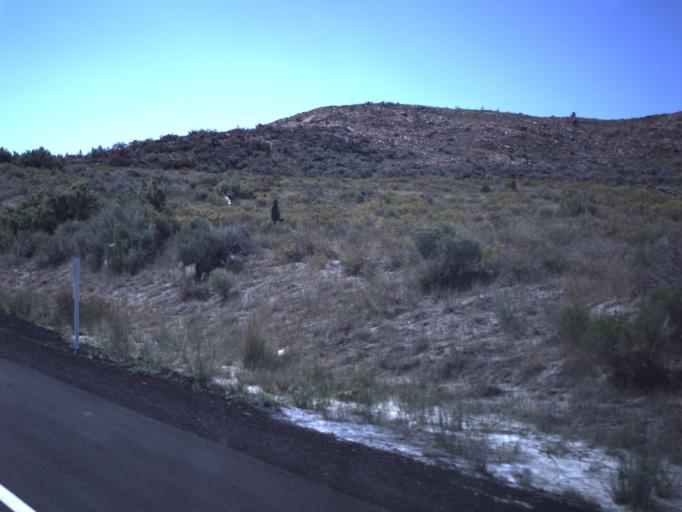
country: US
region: Utah
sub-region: Utah County
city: Eagle Mountain
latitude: 39.9972
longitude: -112.2721
